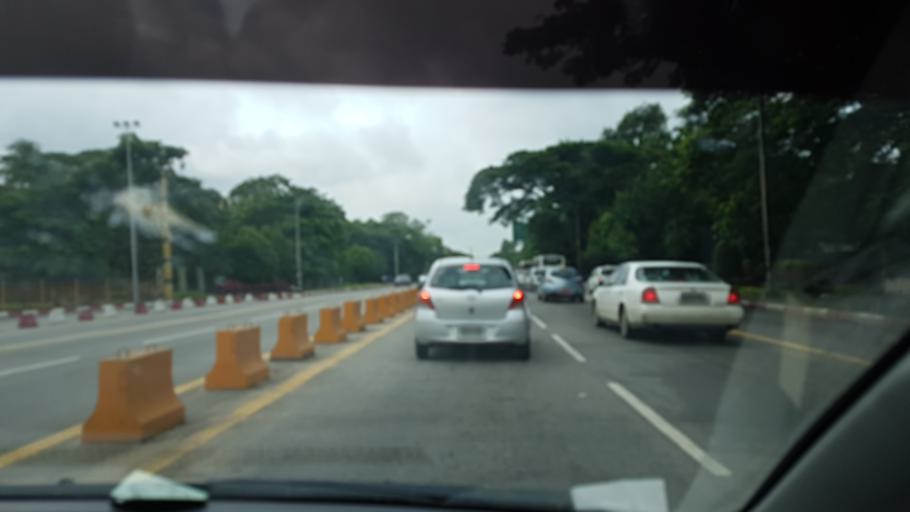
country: MM
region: Yangon
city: Yangon
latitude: 16.7952
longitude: 96.1397
